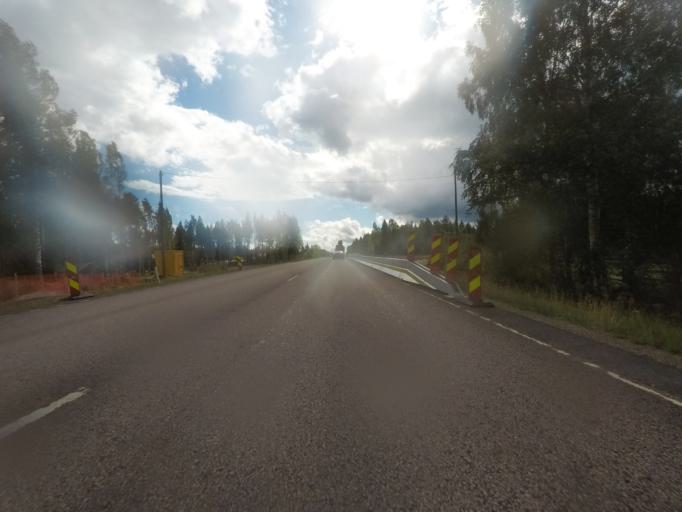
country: FI
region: Central Finland
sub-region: Joutsa
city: Leivonmaeki
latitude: 61.8949
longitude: 26.1146
